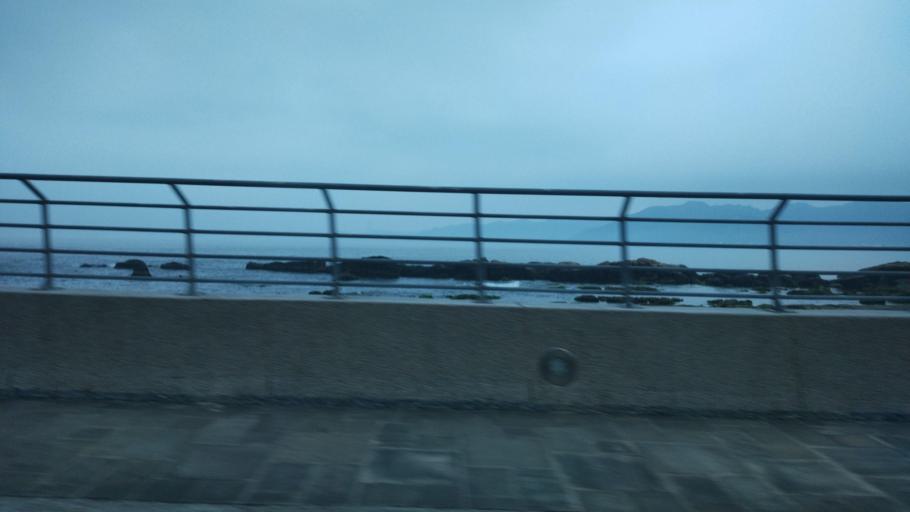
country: TW
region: Taiwan
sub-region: Keelung
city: Keelung
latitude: 25.2007
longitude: 121.6925
